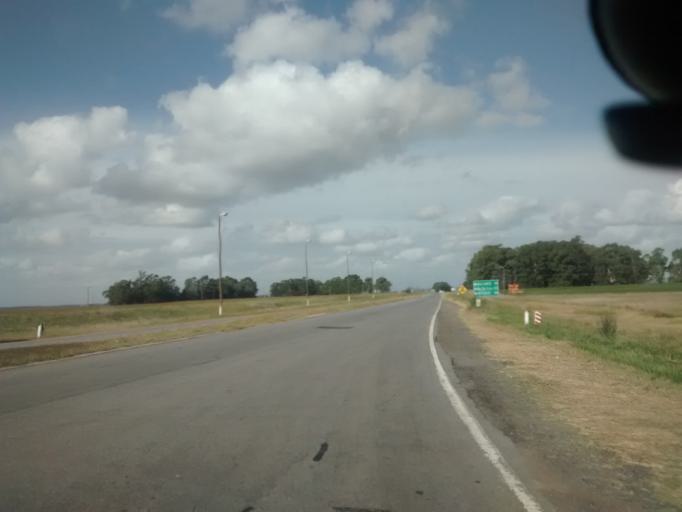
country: AR
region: Buenos Aires
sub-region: Partido de Tandil
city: Tandil
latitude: -37.5823
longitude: -58.7501
